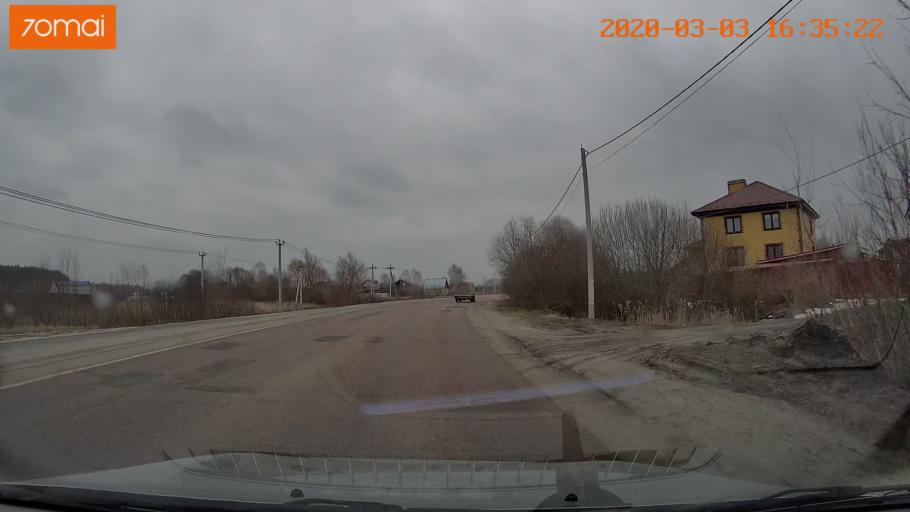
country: RU
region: Moskovskaya
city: Lopatinskiy
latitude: 55.4049
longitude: 38.7641
